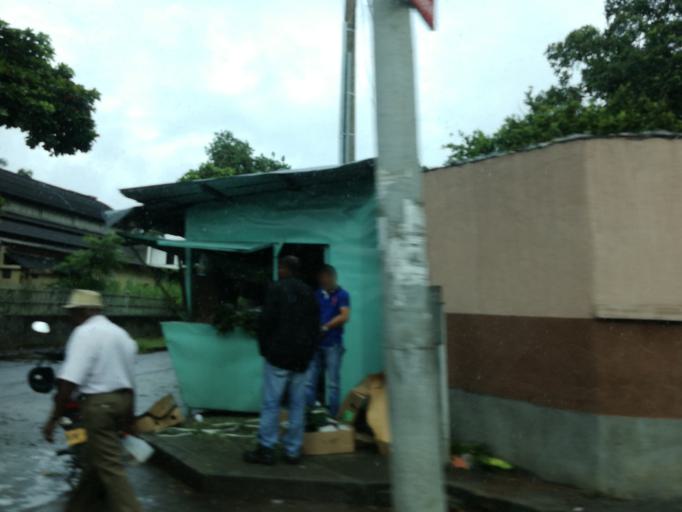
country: CO
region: Valle del Cauca
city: Palmira
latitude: 3.5210
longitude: -76.3036
